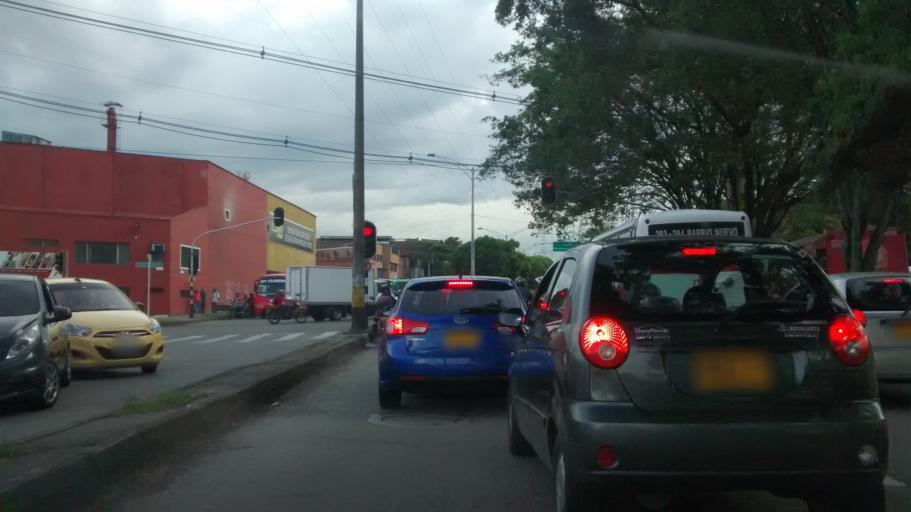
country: CO
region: Antioquia
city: Medellin
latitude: 6.2759
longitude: -75.5735
